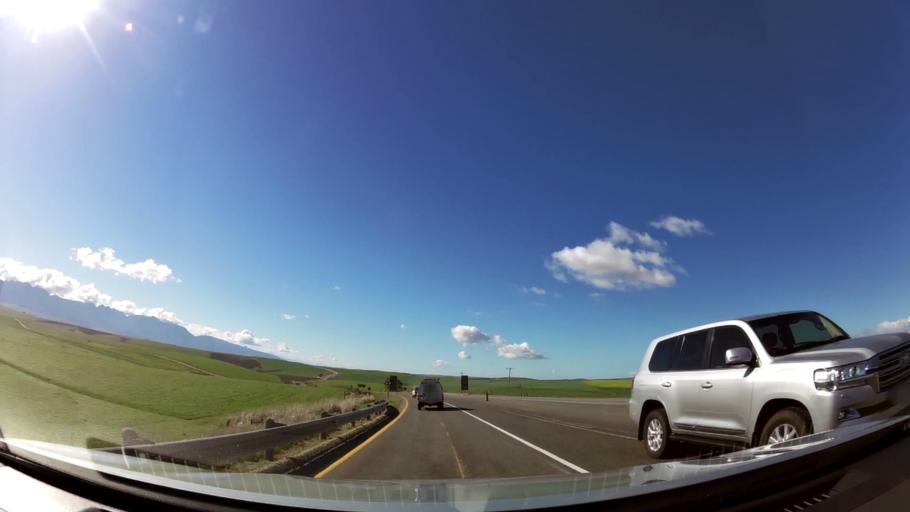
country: ZA
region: Western Cape
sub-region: Overberg District Municipality
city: Caledon
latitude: -34.2017
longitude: 19.6150
